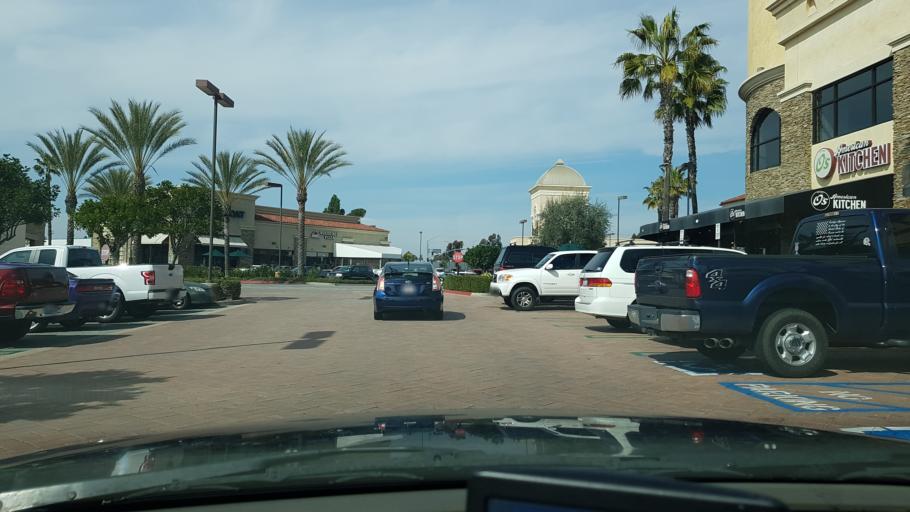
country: US
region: California
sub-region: San Diego County
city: Lake San Marcos
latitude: 33.1413
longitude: -117.1913
